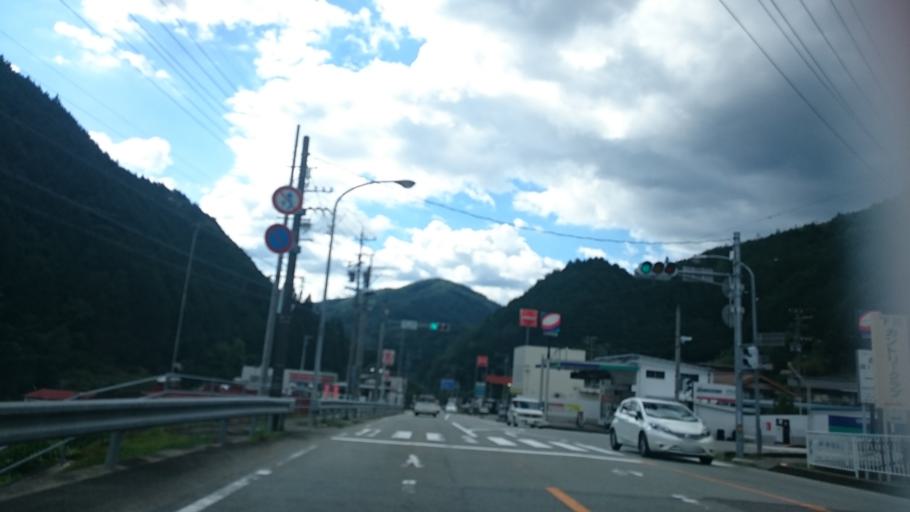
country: JP
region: Gifu
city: Gujo
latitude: 35.7682
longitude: 137.2833
